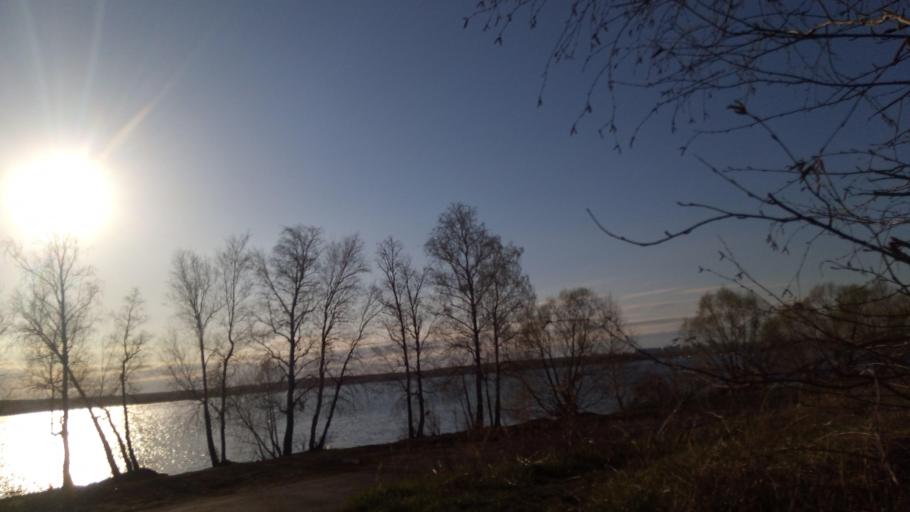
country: RU
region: Chelyabinsk
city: Novosineglazovskiy
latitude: 55.1302
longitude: 61.3285
